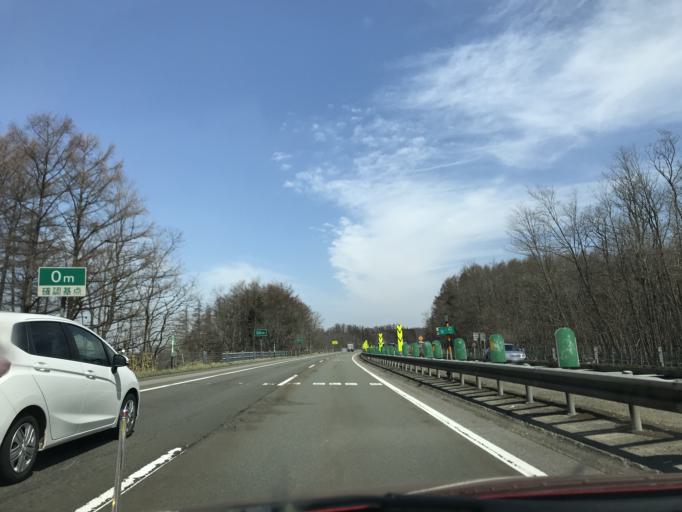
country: JP
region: Hokkaido
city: Bibai
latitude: 43.2773
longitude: 141.8512
